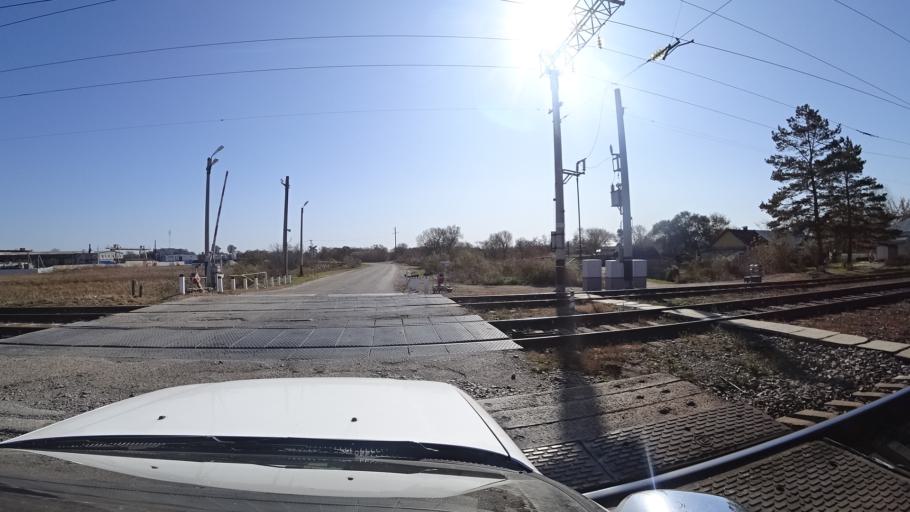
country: RU
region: Primorskiy
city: Dal'nerechensk
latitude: 45.9121
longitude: 133.7945
